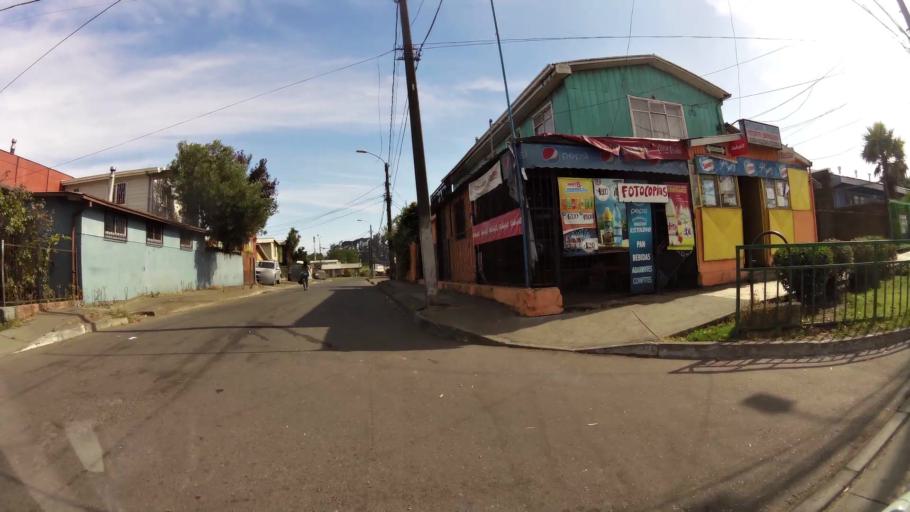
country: CL
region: Biobio
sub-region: Provincia de Concepcion
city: Talcahuano
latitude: -36.7802
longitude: -73.1064
